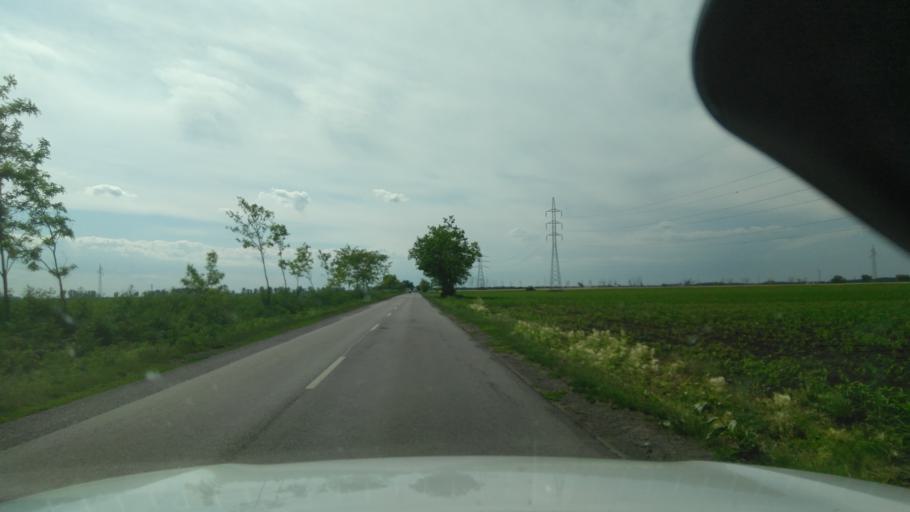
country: HU
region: Bekes
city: Medgyesegyhaza
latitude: 46.5071
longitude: 21.0042
